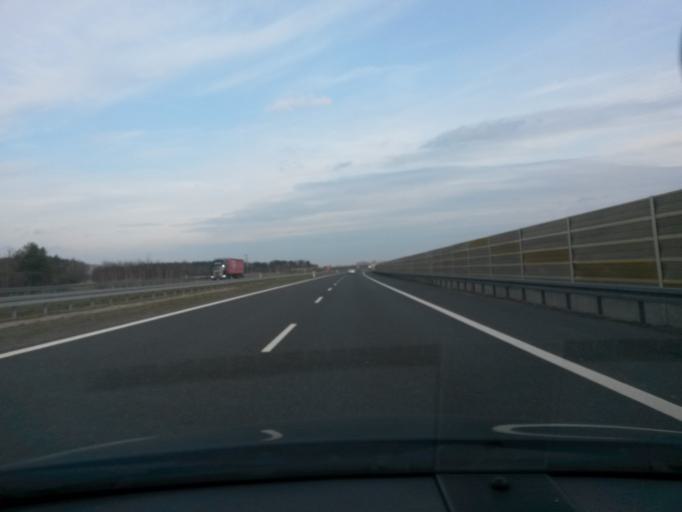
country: PL
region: Lodz Voivodeship
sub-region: Powiat zgierski
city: Parzeczew
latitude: 51.9523
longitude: 19.1527
